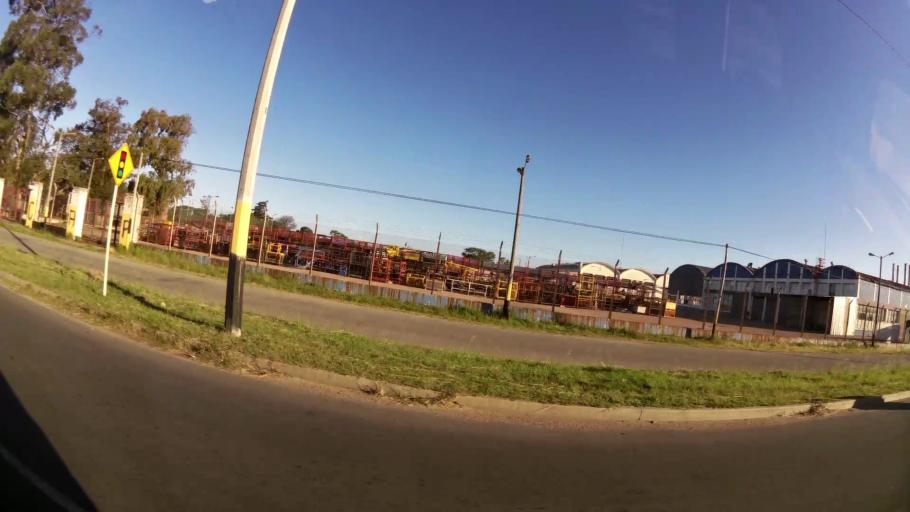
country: UY
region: Canelones
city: Paso de Carrasco
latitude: -34.8578
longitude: -56.0470
